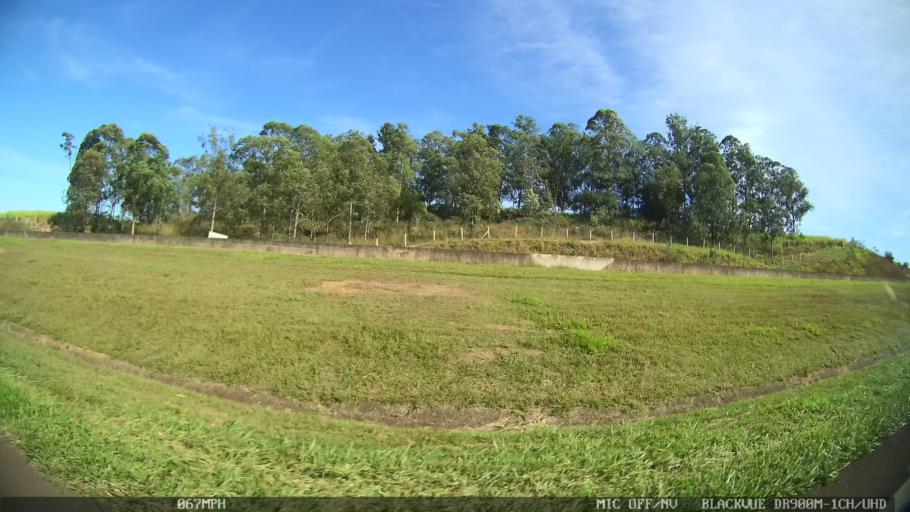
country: BR
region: Sao Paulo
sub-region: Araras
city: Araras
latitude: -22.3328
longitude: -47.3890
